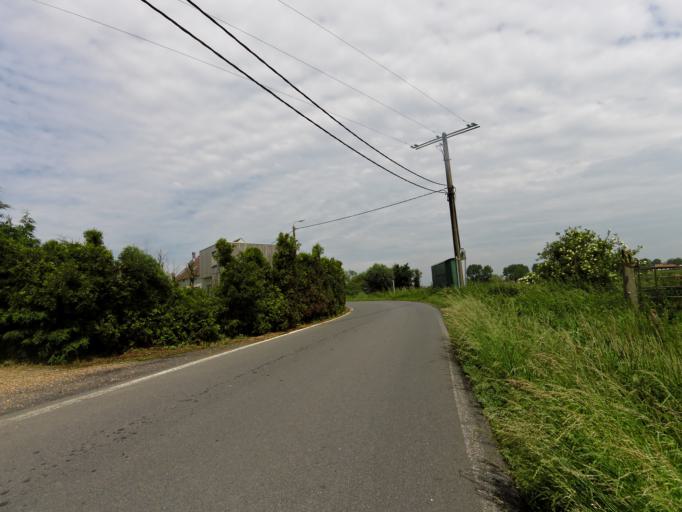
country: BE
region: Flanders
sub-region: Provincie West-Vlaanderen
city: Middelkerke
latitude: 51.1494
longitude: 2.8015
